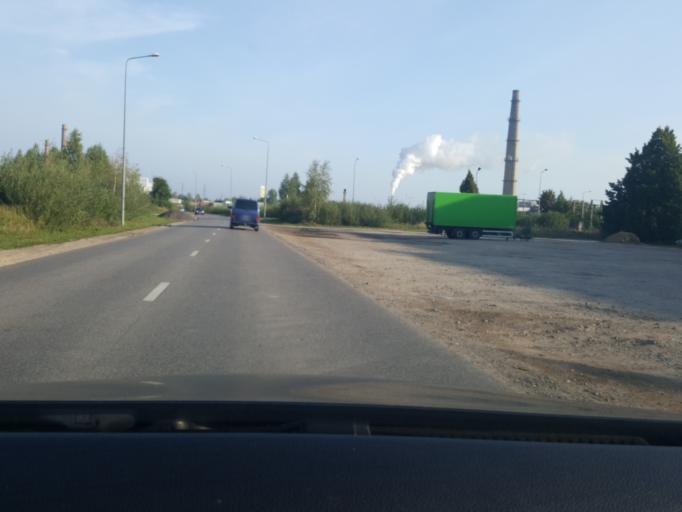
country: LT
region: Alytaus apskritis
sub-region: Alytus
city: Alytus
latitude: 54.4341
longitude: 24.0189
